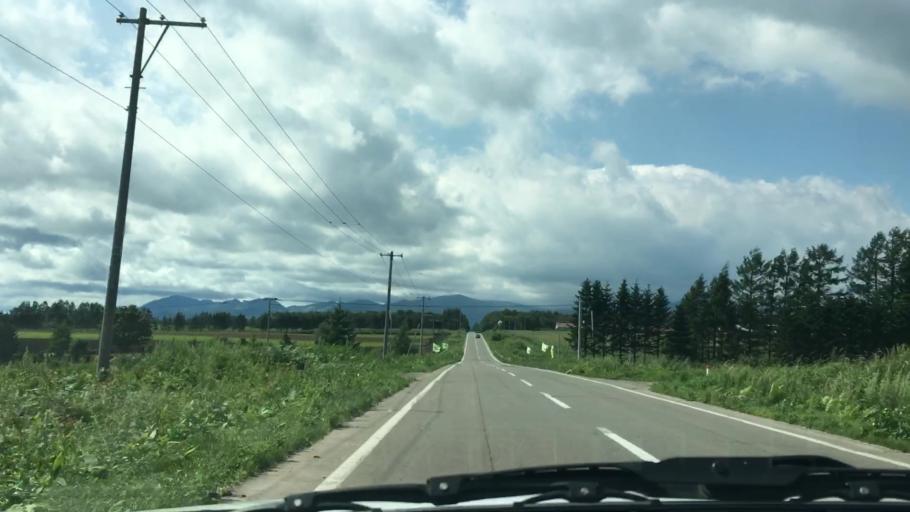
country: JP
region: Hokkaido
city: Otofuke
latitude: 43.2760
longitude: 143.3755
